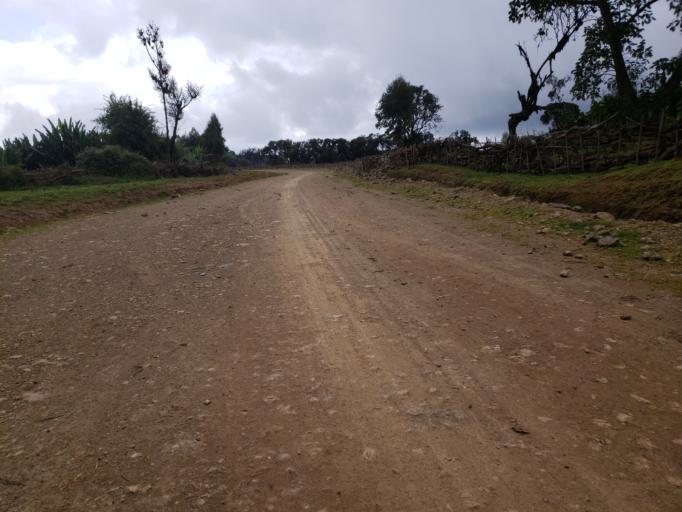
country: ET
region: Oromiya
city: Dodola
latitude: 6.7110
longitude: 39.3740
